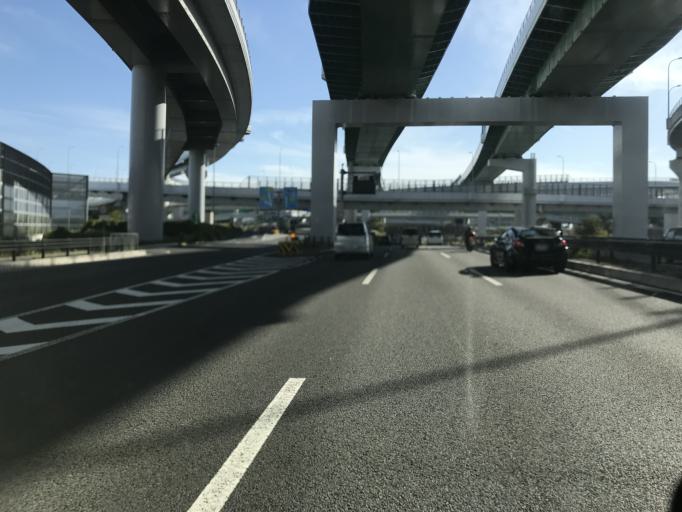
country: JP
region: Aichi
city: Iwakura
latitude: 35.2237
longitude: 136.8542
